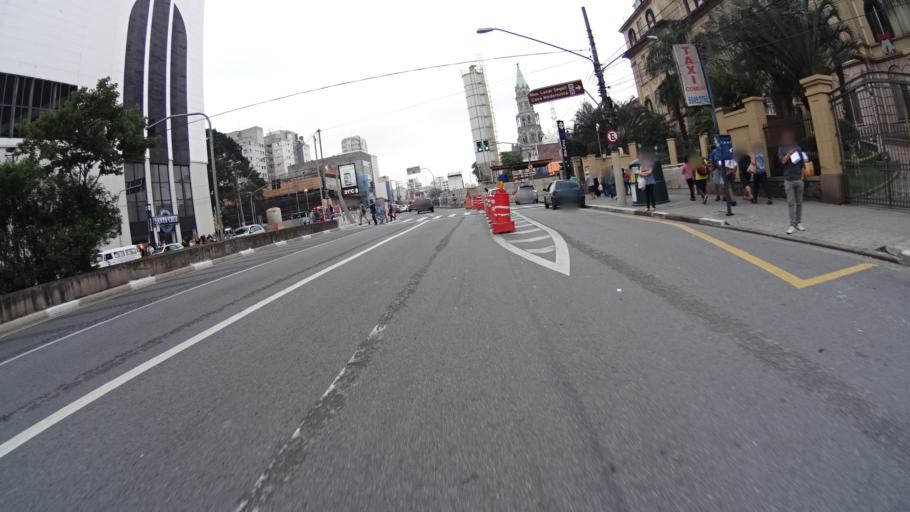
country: BR
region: Sao Paulo
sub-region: Sao Paulo
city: Sao Paulo
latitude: -23.5992
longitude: -46.6365
